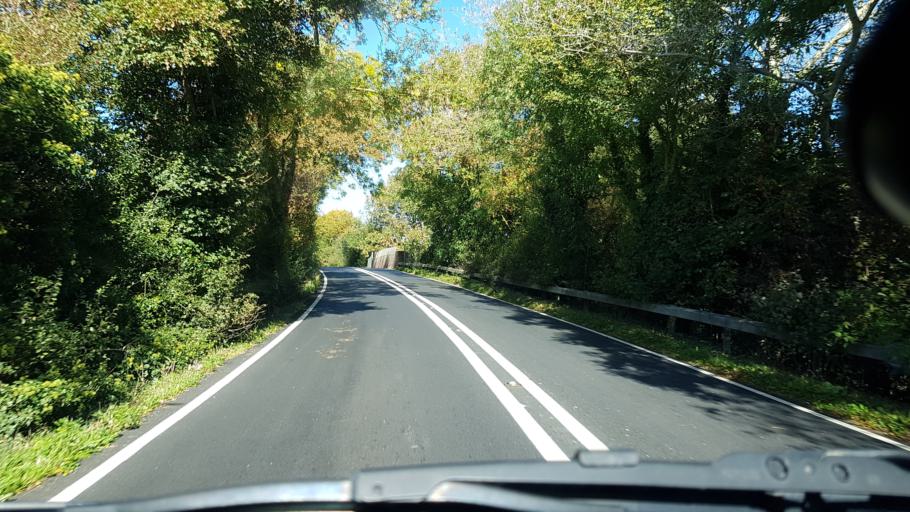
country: GB
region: England
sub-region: West Sussex
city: Billingshurst
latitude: 51.0145
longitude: -0.4349
